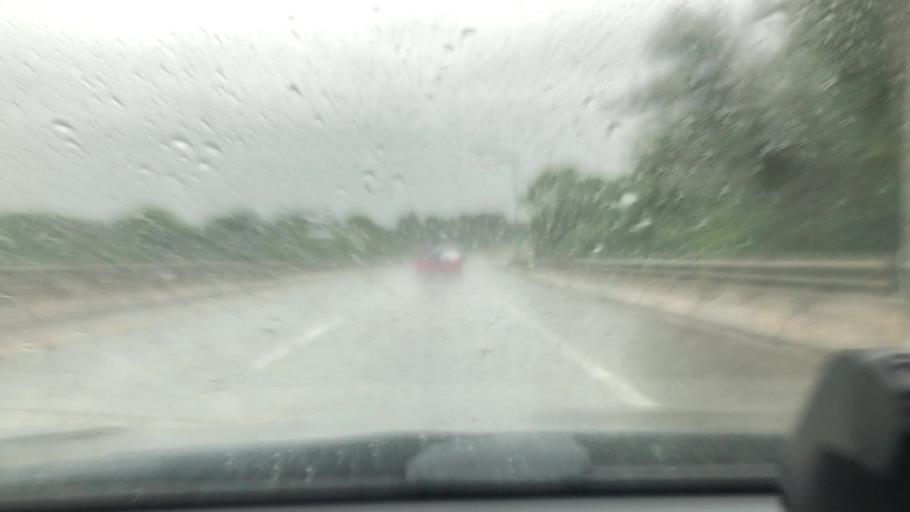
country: US
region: Pennsylvania
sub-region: Northampton County
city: Tatamy
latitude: 40.7510
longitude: -75.2654
